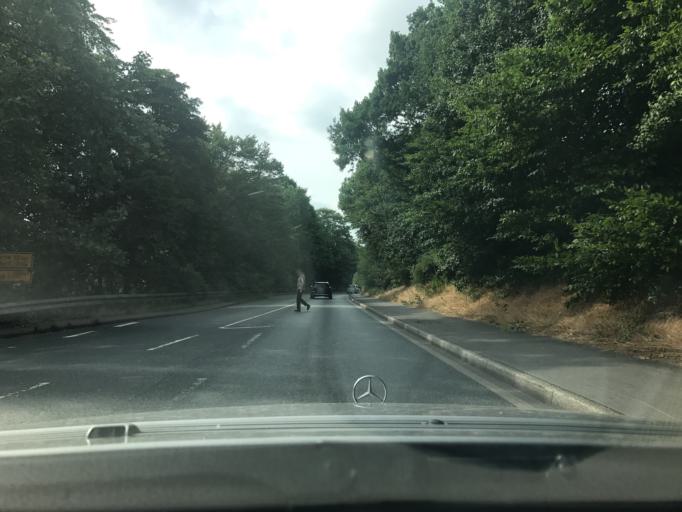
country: DE
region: North Rhine-Westphalia
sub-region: Regierungsbezirk Arnsberg
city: Frondenberg
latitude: 51.4749
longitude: 7.7087
